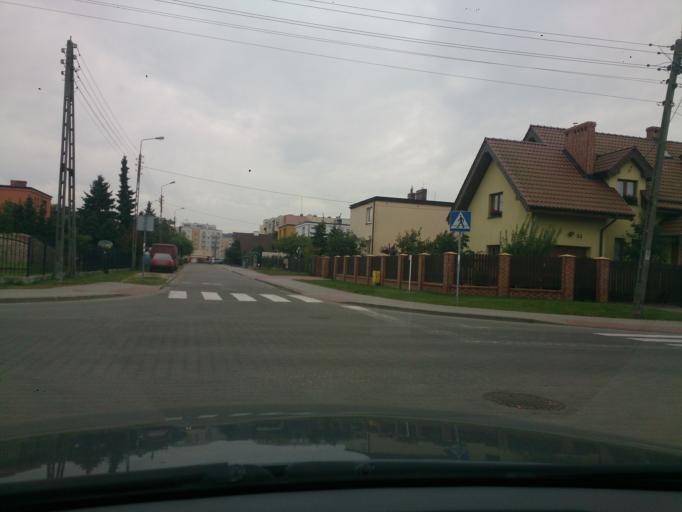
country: PL
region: Pomeranian Voivodeship
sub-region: Powiat wejherowski
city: Reda
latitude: 54.5992
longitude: 18.3610
